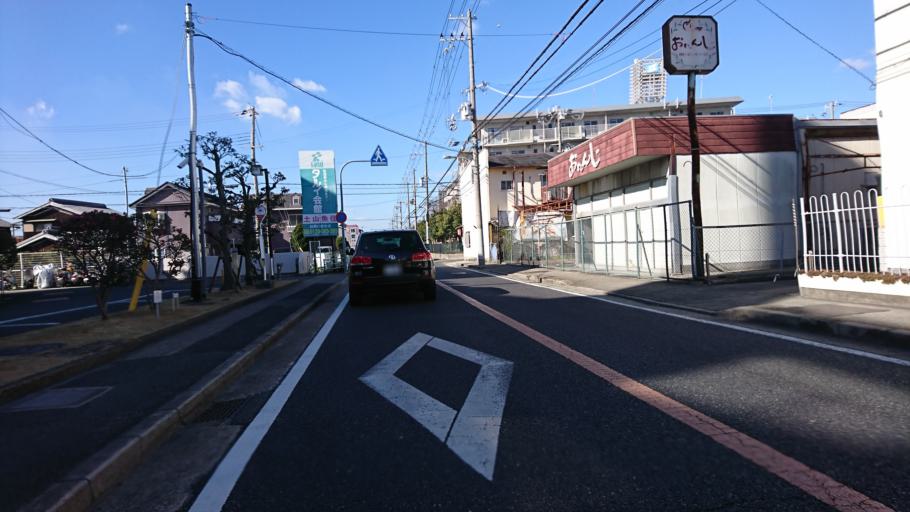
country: JP
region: Hyogo
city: Kakogawacho-honmachi
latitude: 34.7014
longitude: 134.8796
